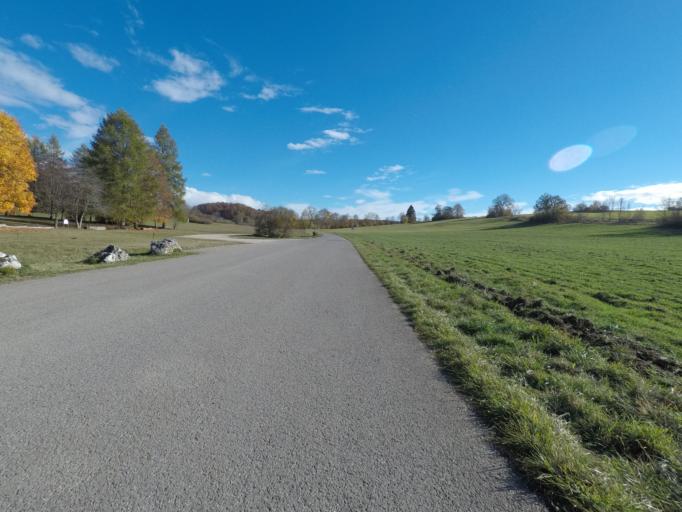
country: DE
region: Baden-Wuerttemberg
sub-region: Tuebingen Region
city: Pfullingen
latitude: 48.4123
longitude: 9.2386
